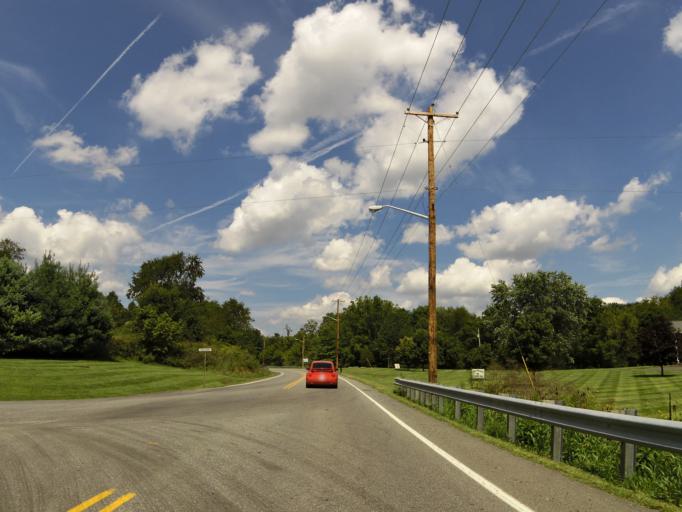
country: US
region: Virginia
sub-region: Washington County
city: Abingdon
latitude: 36.6929
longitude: -81.9749
